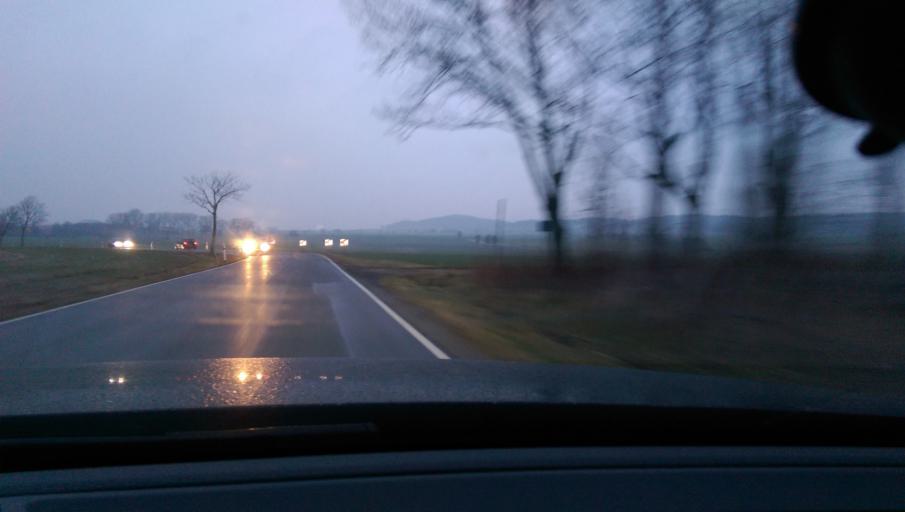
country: DE
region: Lower Saxony
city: Wennigsen
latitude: 52.2902
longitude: 9.5697
